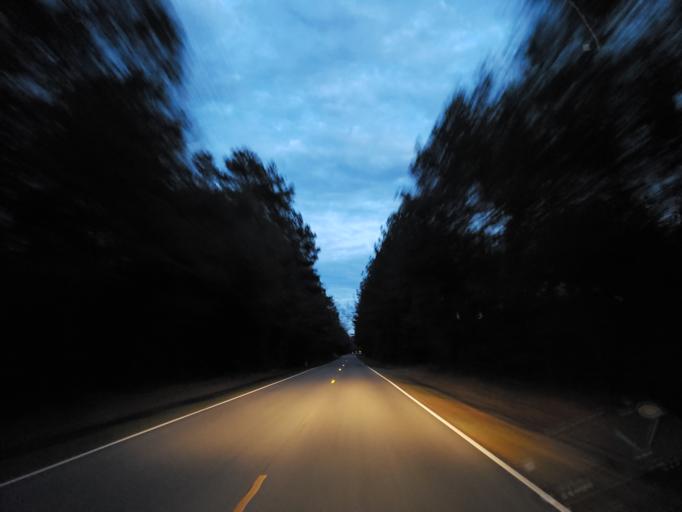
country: US
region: Mississippi
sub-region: Forrest County
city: Hattiesburg
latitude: 31.2454
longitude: -89.2230
